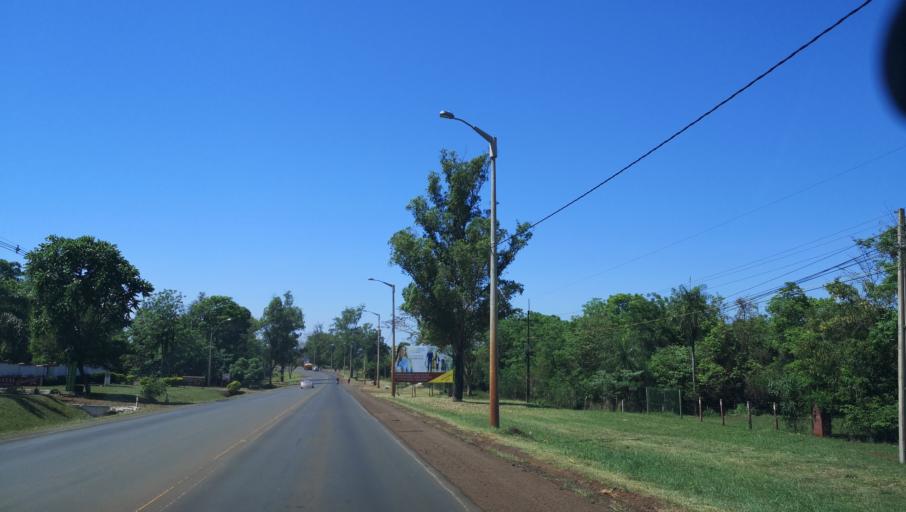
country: PY
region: Itapua
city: San Juan del Parana
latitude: -27.2902
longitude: -55.9357
